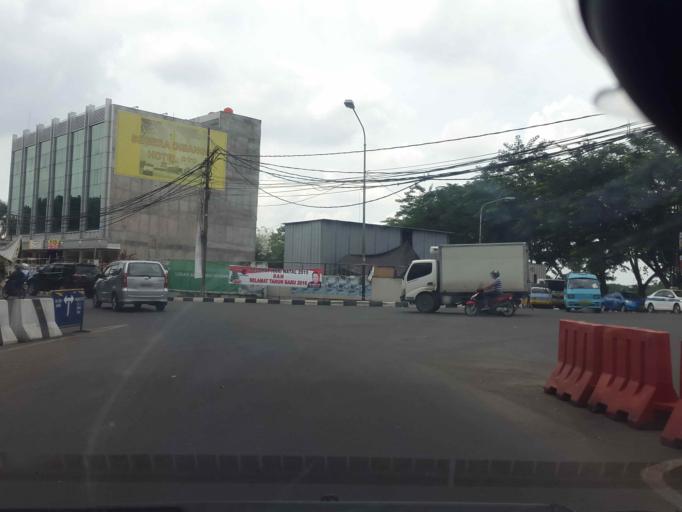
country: ID
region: Banten
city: Tangerang
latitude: -6.1692
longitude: 106.6337
